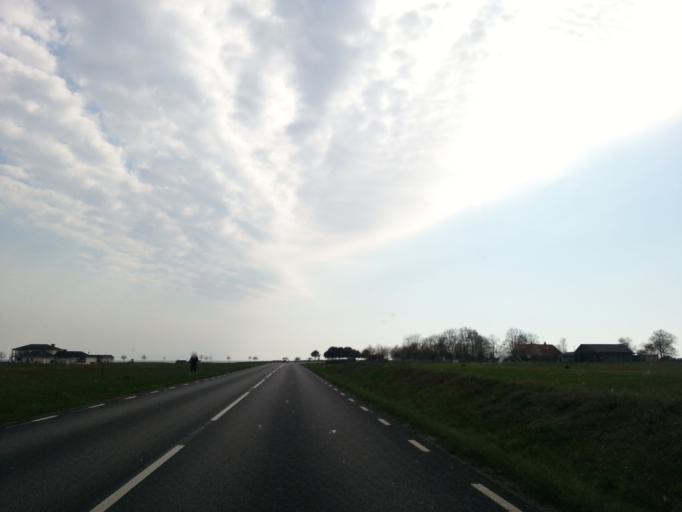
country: SE
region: Skane
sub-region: Trelleborgs Kommun
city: Skare
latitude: 55.3721
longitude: 13.0828
